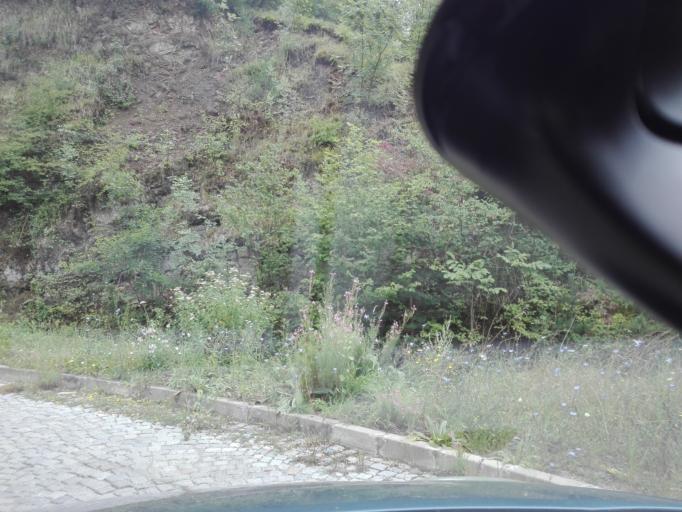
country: BG
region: Sofia-Capital
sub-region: Stolichna Obshtina
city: Sofia
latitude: 42.6055
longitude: 23.3936
